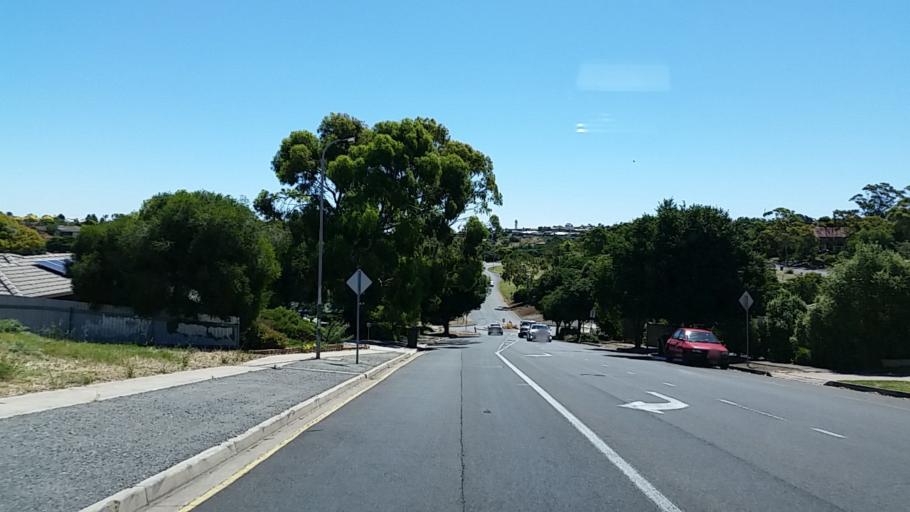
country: AU
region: South Australia
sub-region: Marion
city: Trott Park
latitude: -35.0763
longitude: 138.5364
